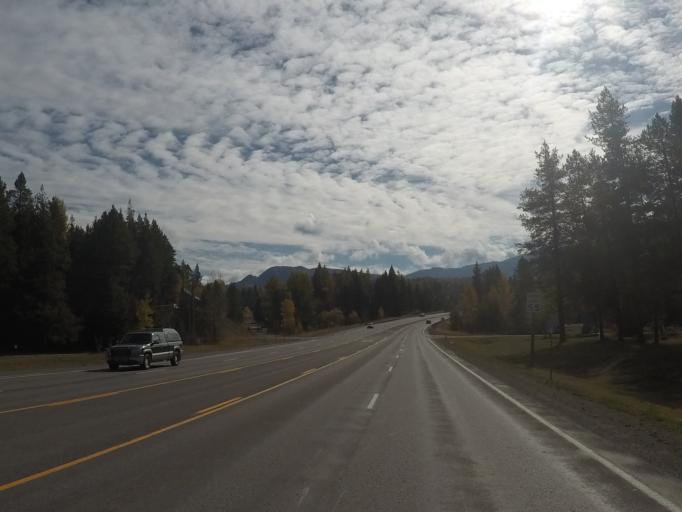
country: US
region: Montana
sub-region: Flathead County
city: Columbia Falls
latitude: 48.3990
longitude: -114.0421
